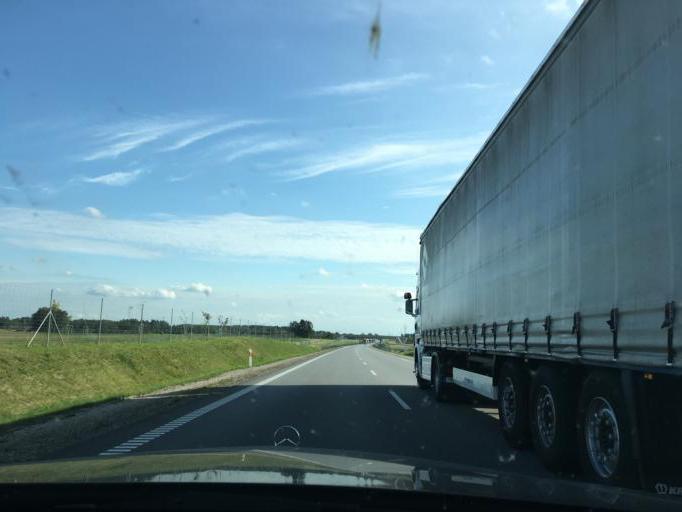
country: PL
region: Podlasie
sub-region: Powiat augustowski
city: Augustow
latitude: 53.8858
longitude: 22.8717
